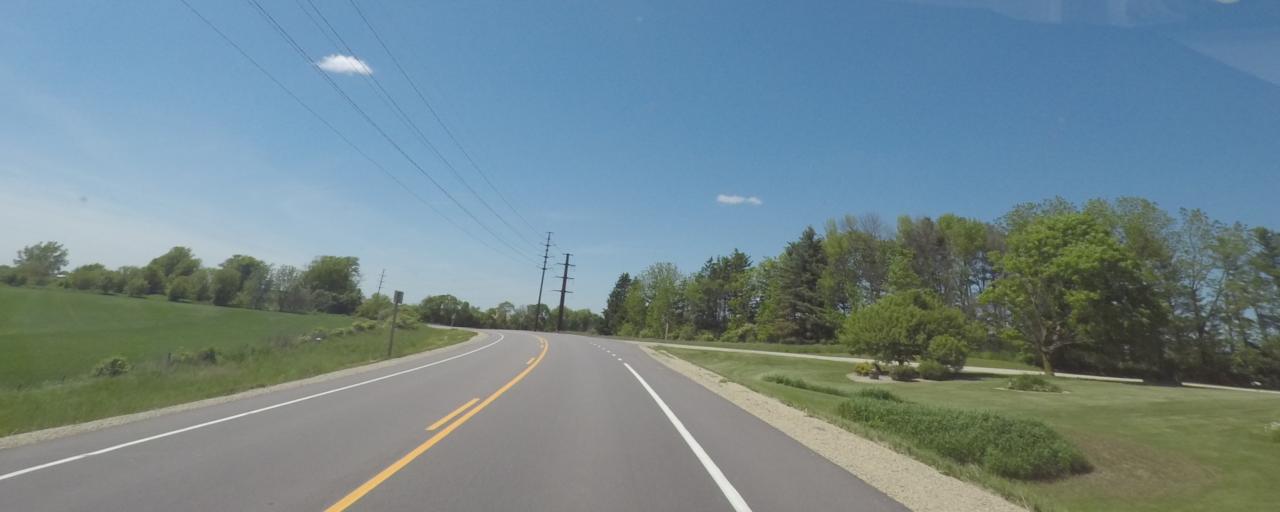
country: US
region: Wisconsin
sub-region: Dane County
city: Fitchburg
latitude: 42.9713
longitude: -89.5003
